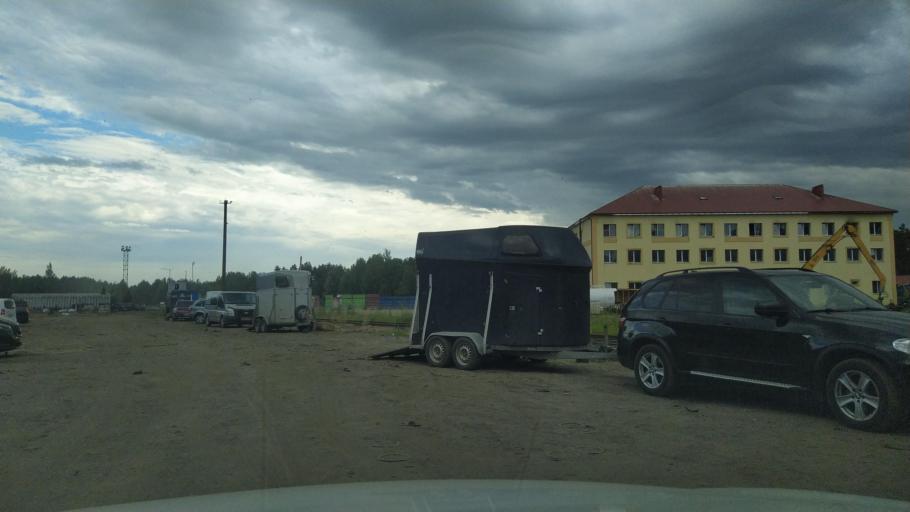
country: RU
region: St.-Petersburg
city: Bol'shaya Izhora
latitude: 59.9167
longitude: 29.5790
